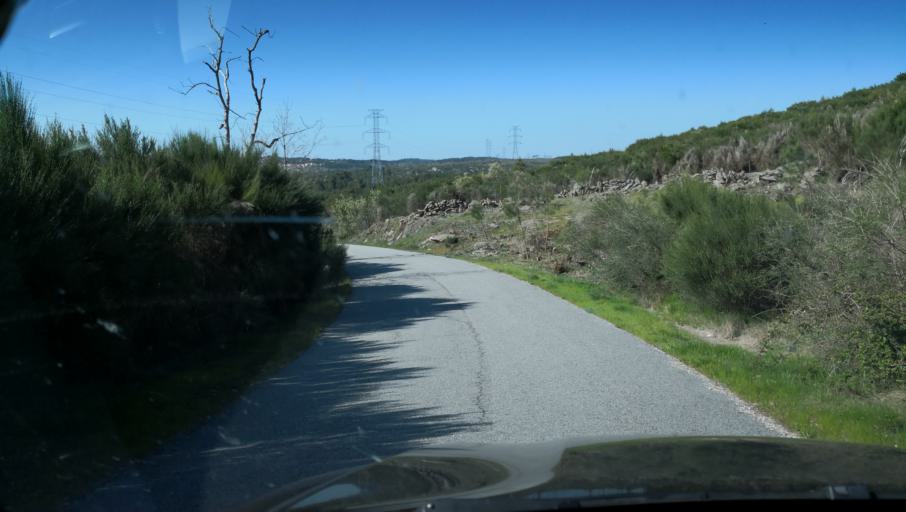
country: PT
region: Vila Real
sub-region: Sabrosa
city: Sabrosa
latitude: 41.2949
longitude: -7.6374
